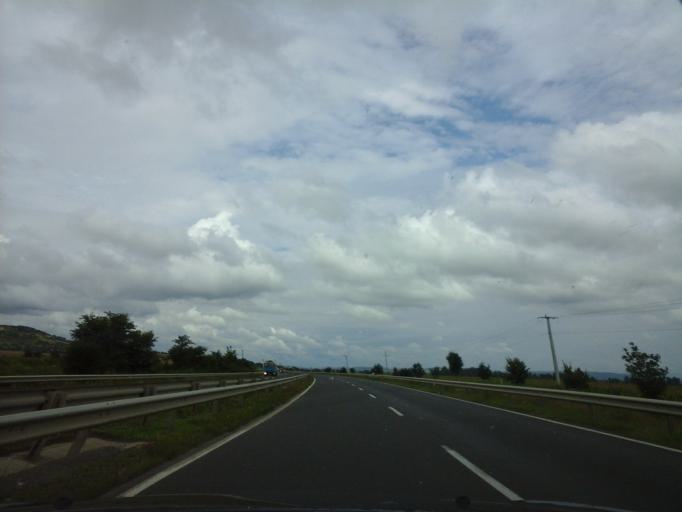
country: HU
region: Borsod-Abauj-Zemplen
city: Sajobabony
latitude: 48.1954
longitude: 20.7475
